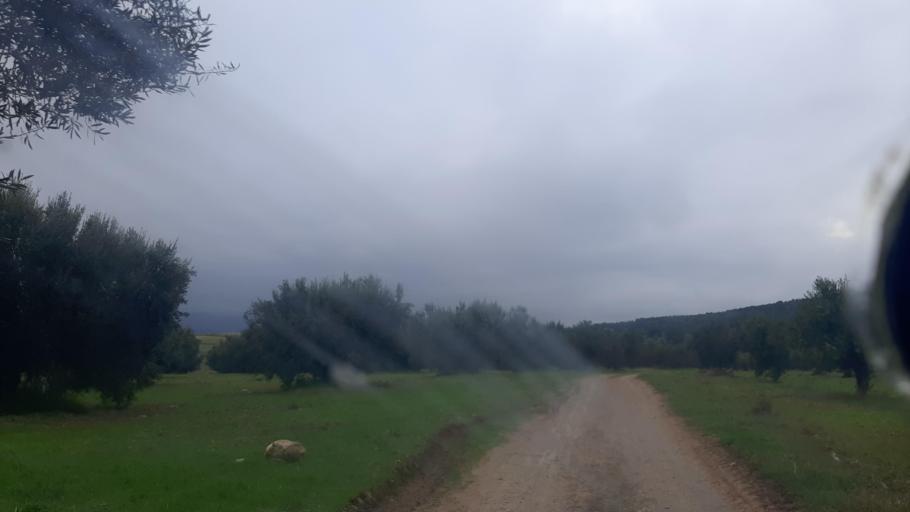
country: TN
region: Tunis
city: La Sebala du Mornag
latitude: 36.5818
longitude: 10.2901
